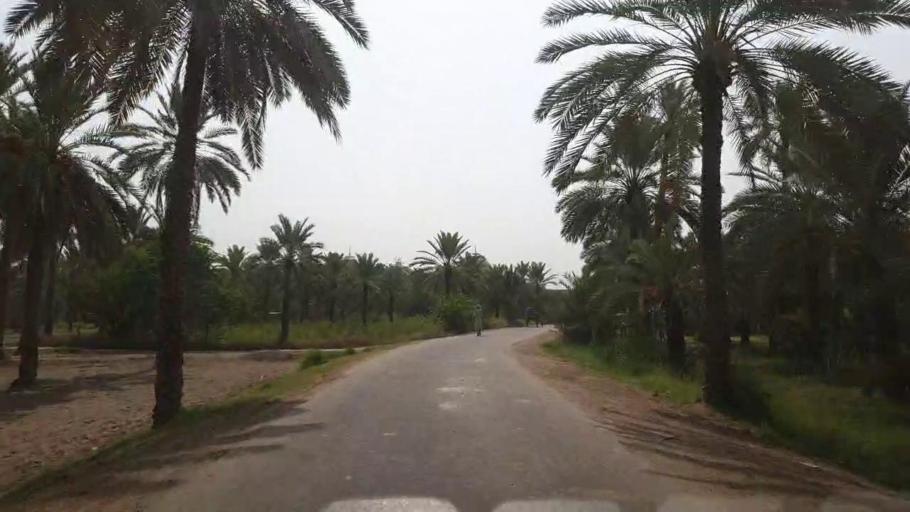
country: PK
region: Sindh
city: Gambat
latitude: 27.4073
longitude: 68.5555
